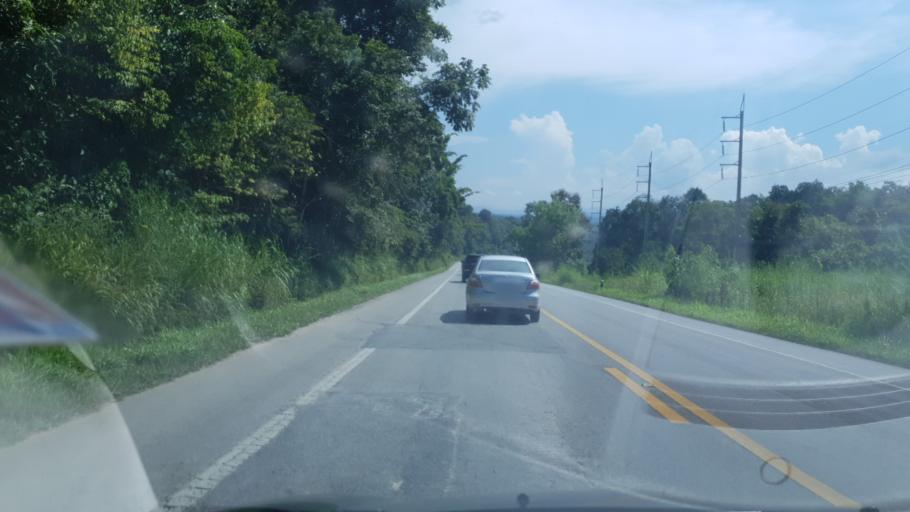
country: TH
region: Chiang Rai
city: Wiang Pa Pao
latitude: 19.4364
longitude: 99.5012
